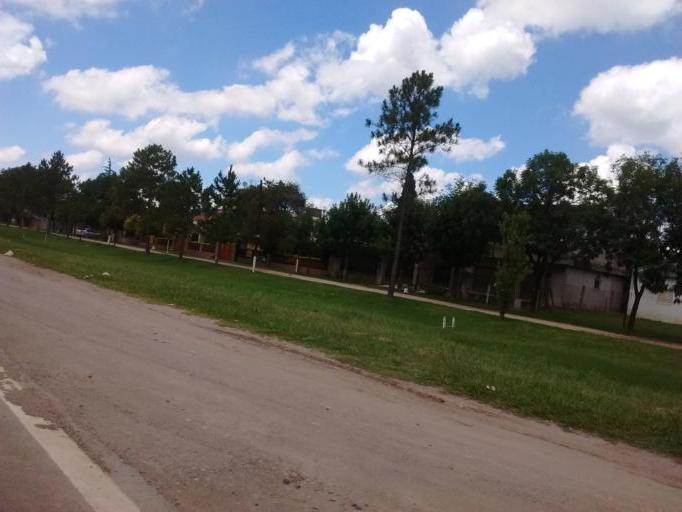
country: AR
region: Santa Fe
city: Funes
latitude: -32.9237
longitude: -60.7889
